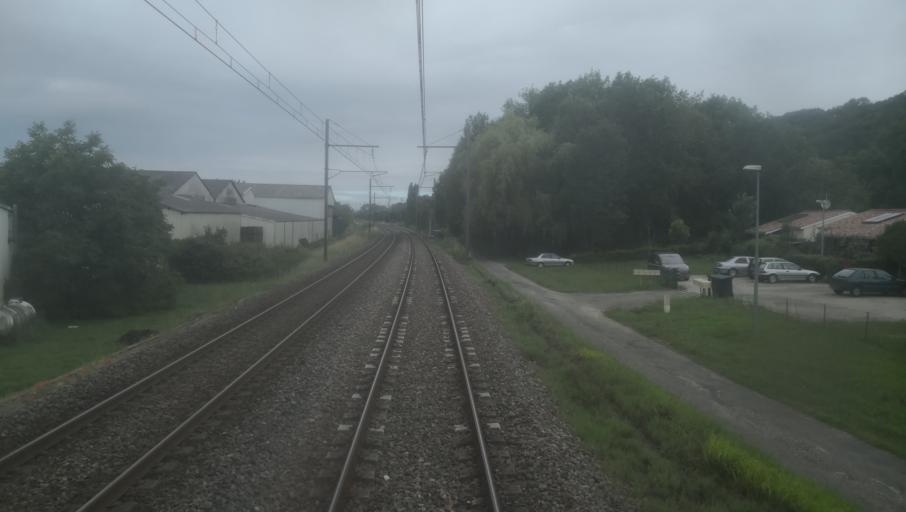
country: FR
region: Aquitaine
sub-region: Departement du Lot-et-Garonne
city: Port-Sainte-Marie
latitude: 44.2547
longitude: 0.3750
